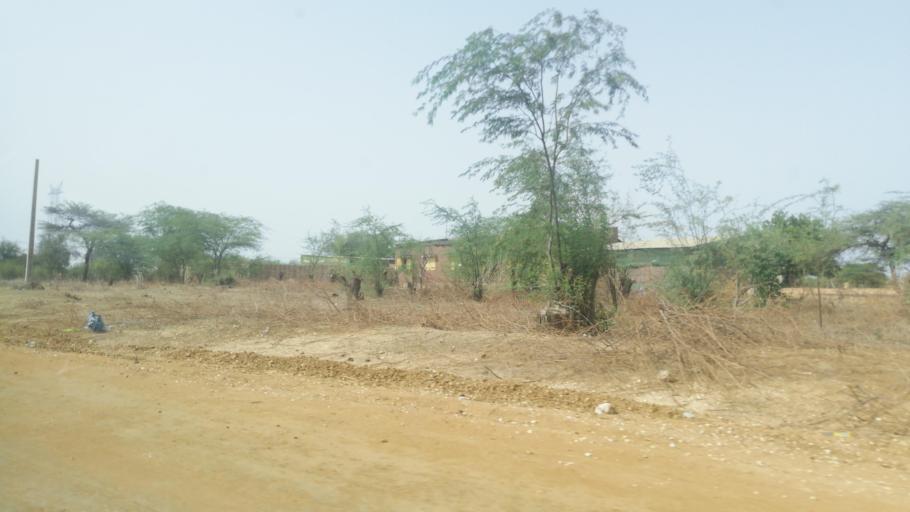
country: SN
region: Saint-Louis
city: Saint-Louis
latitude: 16.0828
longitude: -16.3634
